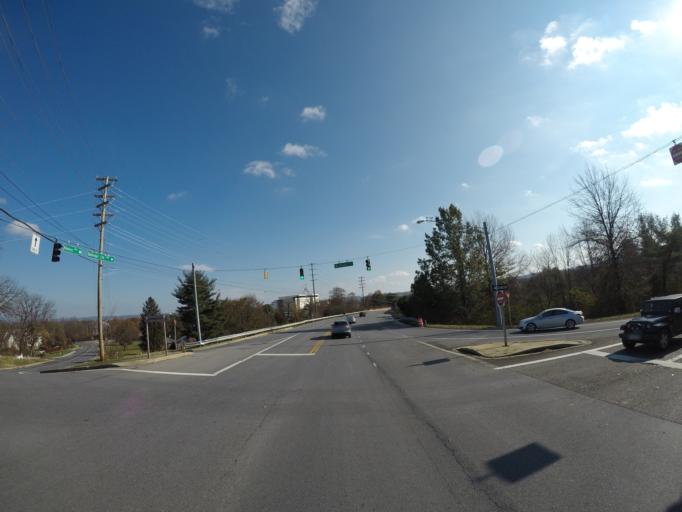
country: US
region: Maryland
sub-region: Frederick County
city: Ballenger Creek
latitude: 39.4030
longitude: -77.4401
